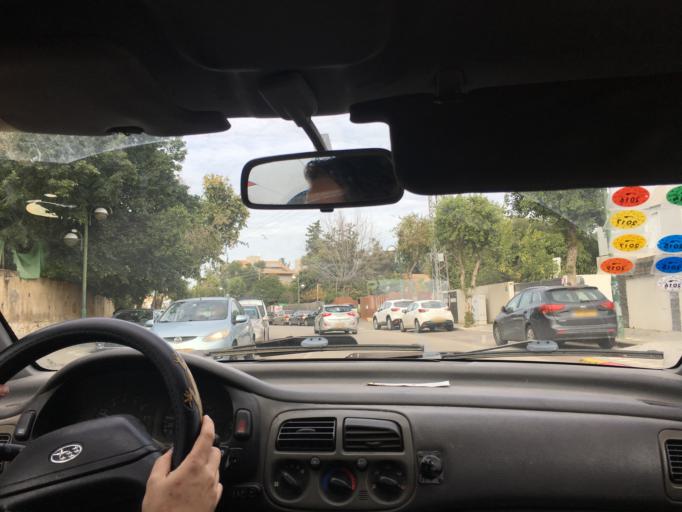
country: IL
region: Tel Aviv
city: Ramat HaSharon
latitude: 32.1353
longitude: 34.8455
